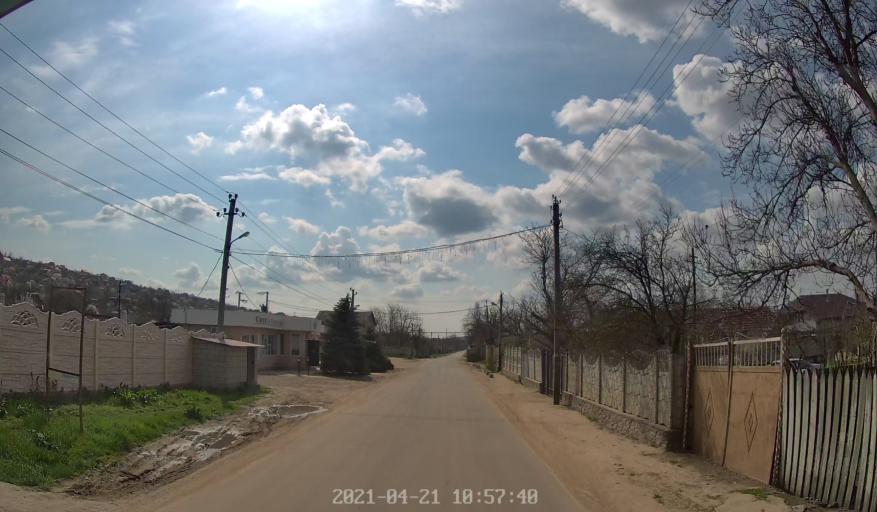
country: MD
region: Chisinau
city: Singera
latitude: 46.9585
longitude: 28.9399
